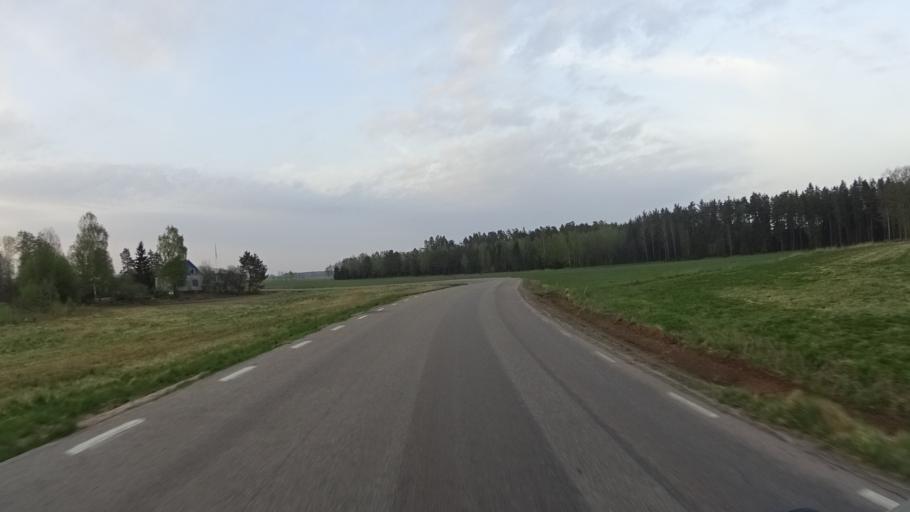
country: SE
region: Vaestra Goetaland
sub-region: Gotene Kommun
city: Kallby
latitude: 58.4824
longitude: 13.3166
